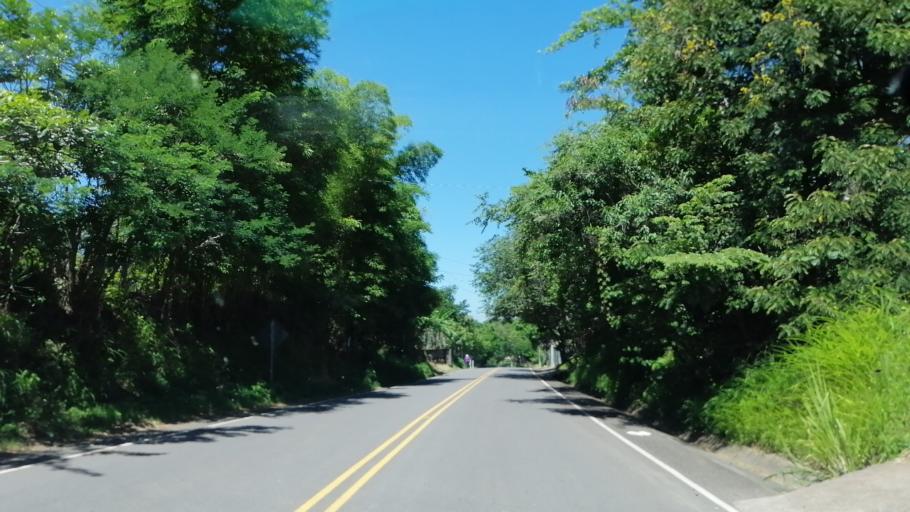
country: SV
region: Morazan
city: Cacaopera
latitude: 13.8147
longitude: -88.1733
